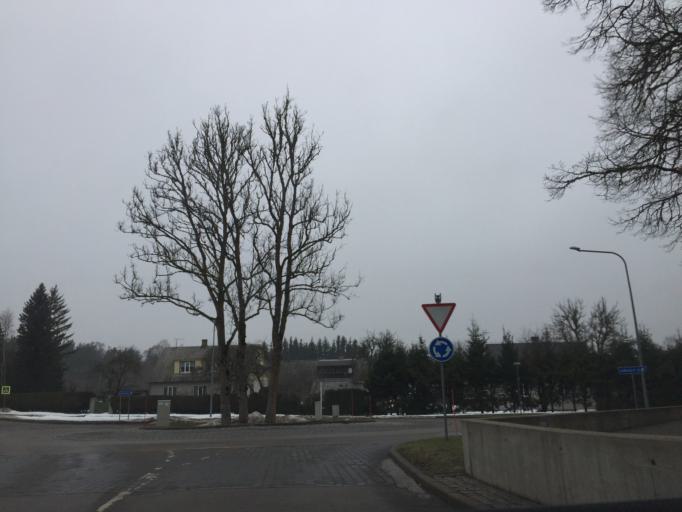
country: EE
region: Saare
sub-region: Kuressaare linn
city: Kuressaare
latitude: 58.4081
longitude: 22.7879
